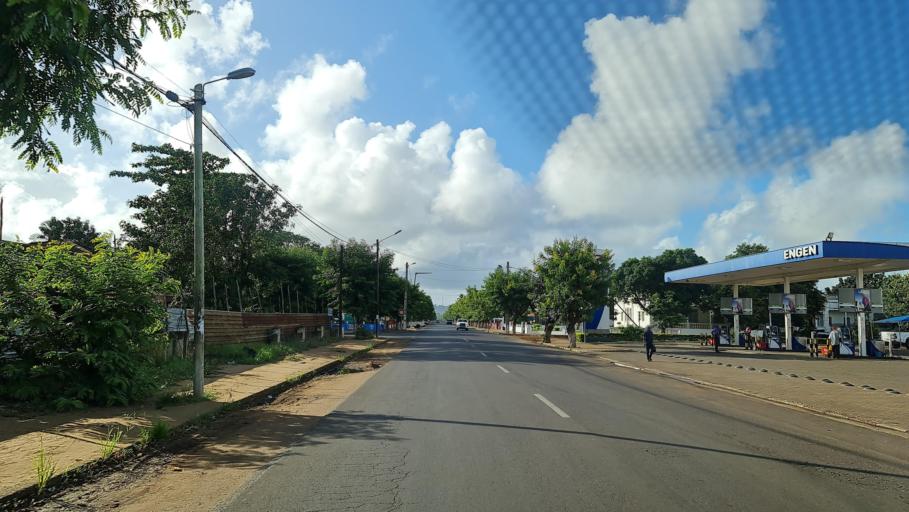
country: MZ
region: Gaza
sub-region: Xai-Xai District
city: Xai-Xai
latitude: -25.0360
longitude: 33.6372
